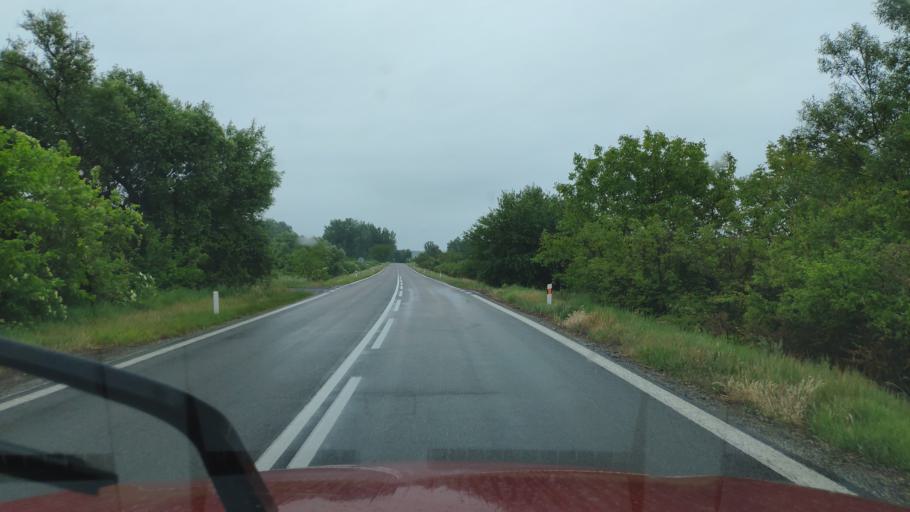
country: HU
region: Borsod-Abauj-Zemplen
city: Ricse
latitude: 48.4332
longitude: 21.8833
